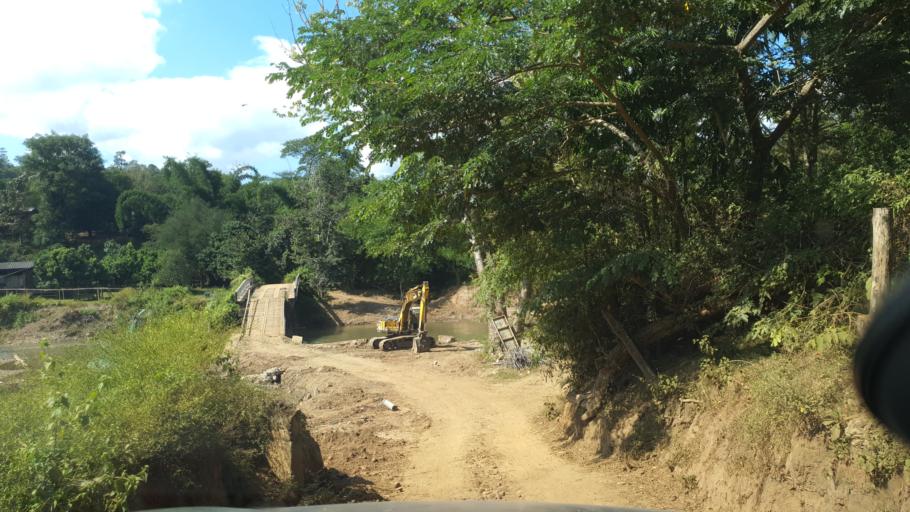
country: TH
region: Mae Hong Son
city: Mae Hi
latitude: 19.2957
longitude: 98.7088
